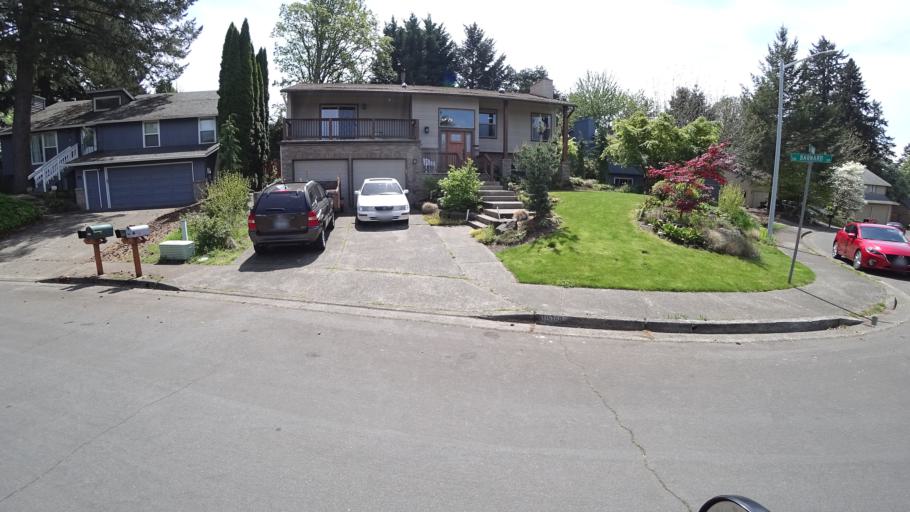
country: US
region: Oregon
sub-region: Washington County
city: Aloha
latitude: 45.4624
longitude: -122.8389
